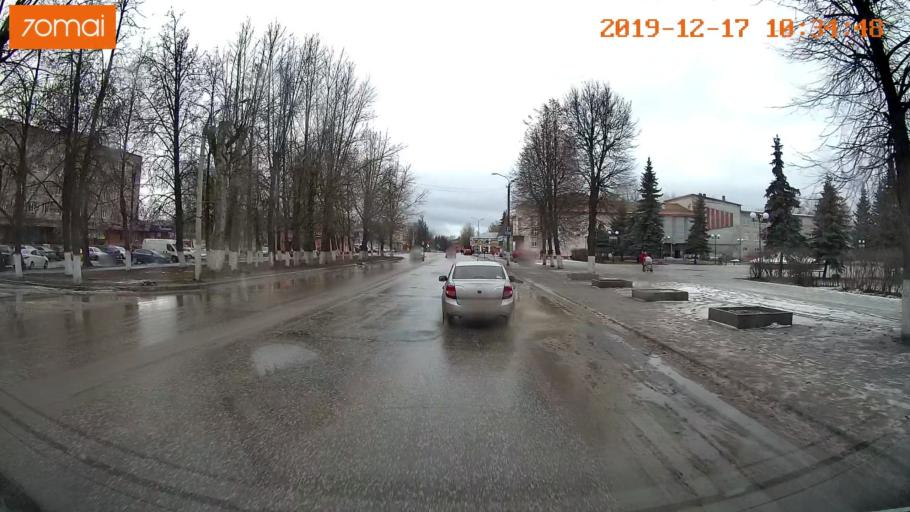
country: RU
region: Vladimir
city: Gus'-Khrustal'nyy
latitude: 55.6165
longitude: 40.6729
